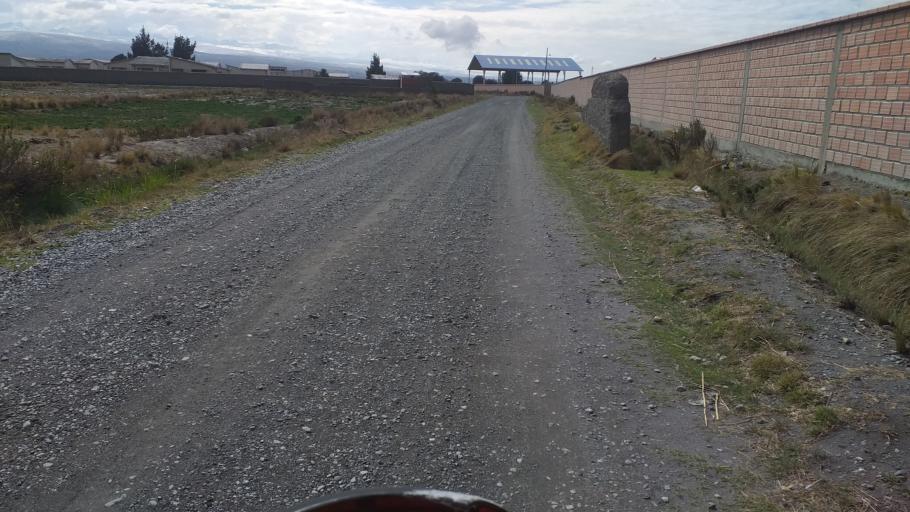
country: BO
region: La Paz
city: Achacachi
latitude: -16.0169
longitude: -68.7038
